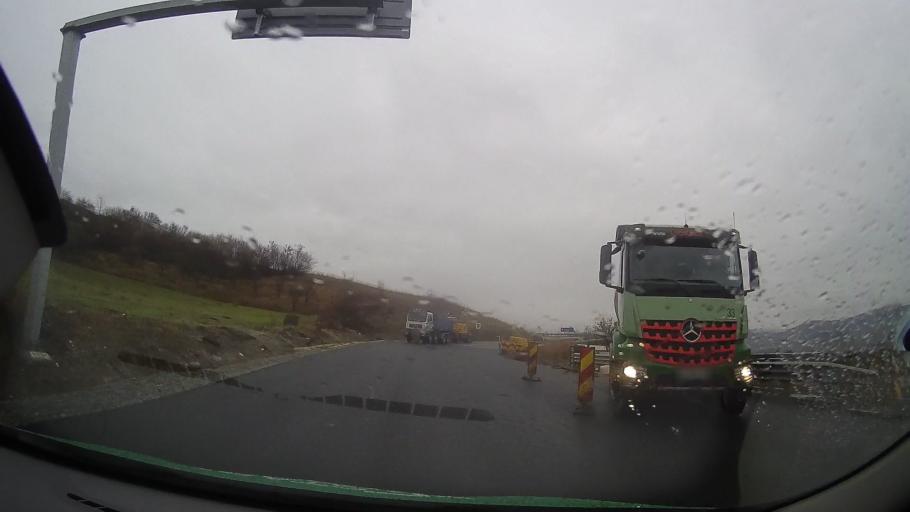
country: RO
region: Bistrita-Nasaud
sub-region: Comuna Teaca
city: Teaca
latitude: 46.9039
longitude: 24.4994
